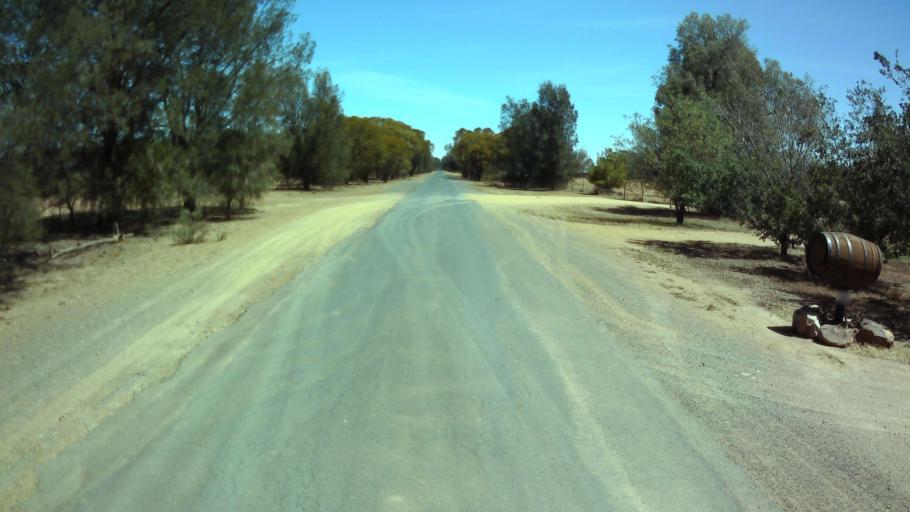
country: AU
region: New South Wales
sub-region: Weddin
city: Grenfell
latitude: -33.8704
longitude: 147.6920
